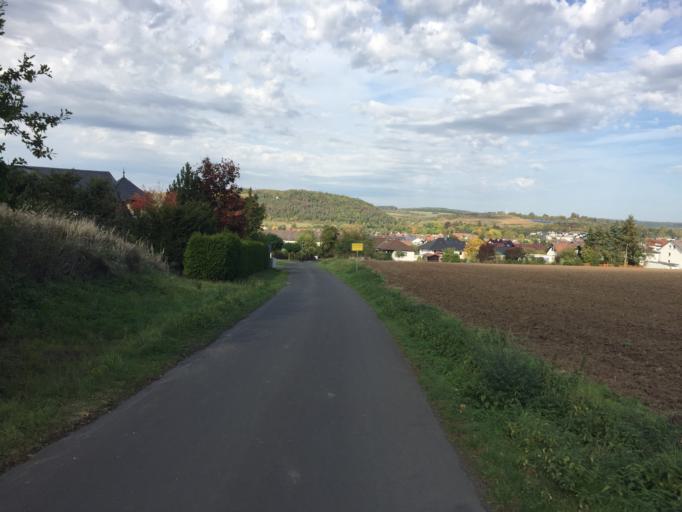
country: DE
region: Hesse
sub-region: Regierungsbezirk Giessen
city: Grossen Buseck
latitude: 50.6011
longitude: 8.7781
